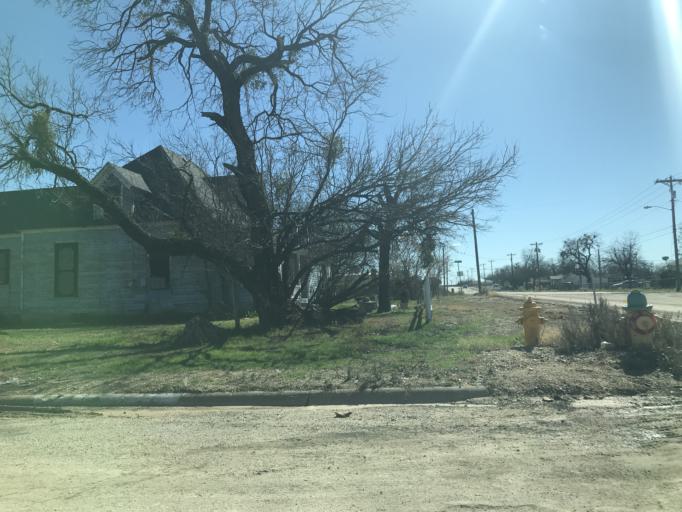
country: US
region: Texas
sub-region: Tom Green County
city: San Angelo
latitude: 31.4643
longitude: -100.4132
